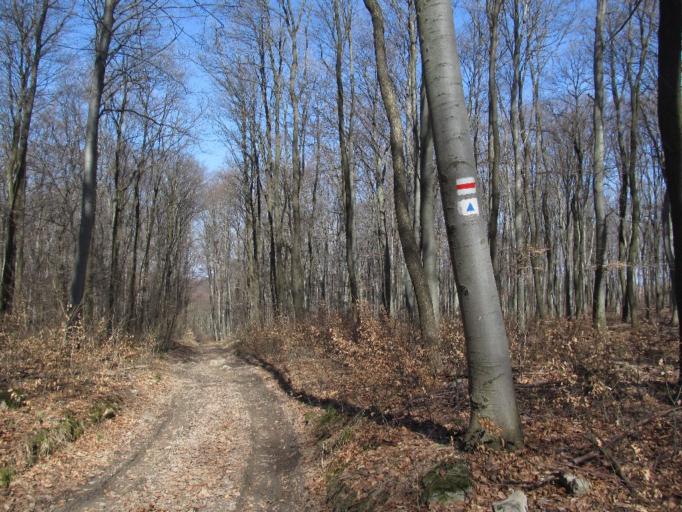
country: HU
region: Fejer
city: Bakonycsernye
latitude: 47.2767
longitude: 18.1061
